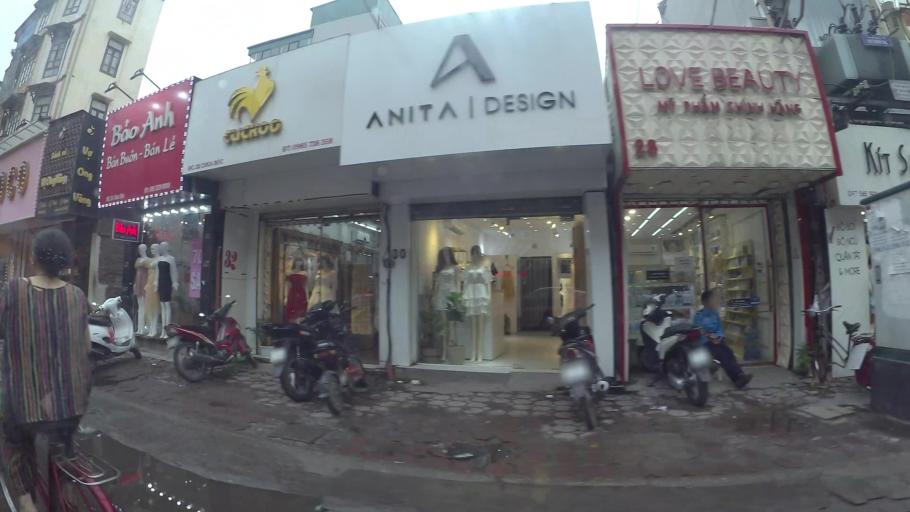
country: VN
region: Ha Noi
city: Dong Da
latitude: 21.0086
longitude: 105.8265
